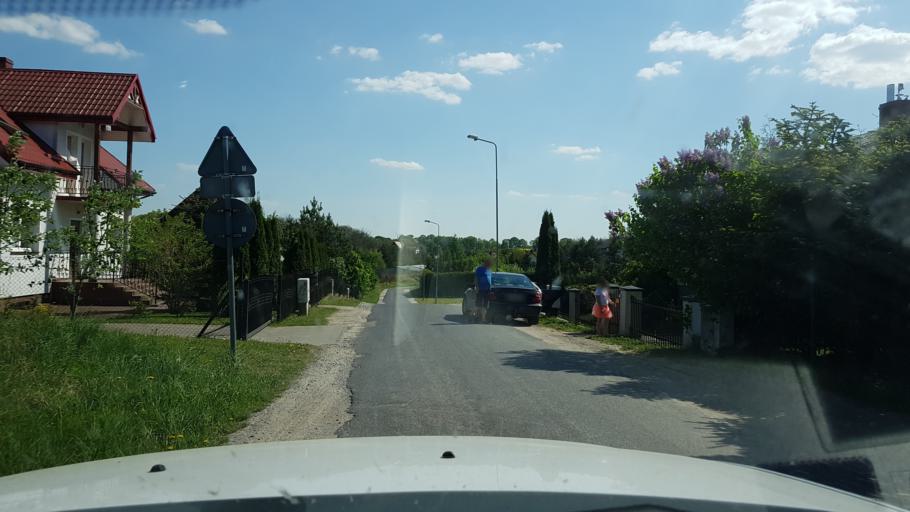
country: PL
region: West Pomeranian Voivodeship
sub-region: Powiat kolobrzeski
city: Goscino
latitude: 54.0528
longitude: 15.6584
